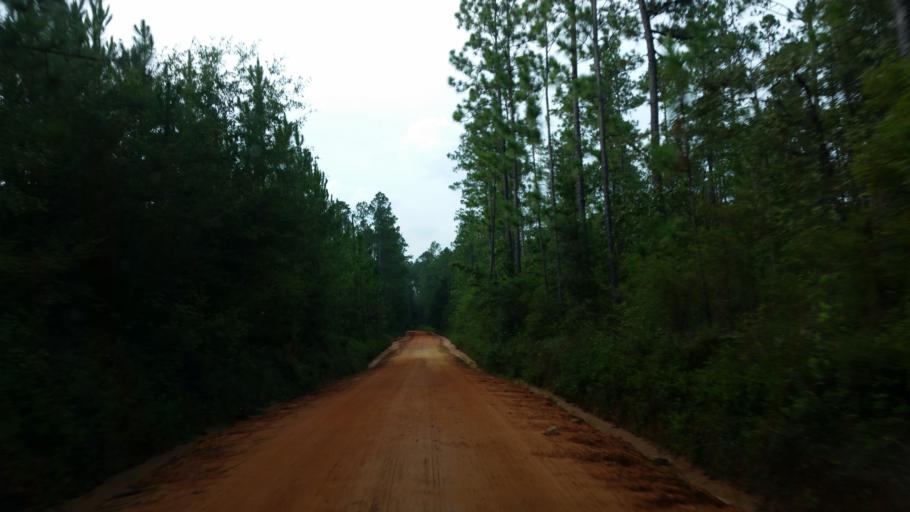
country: US
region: Alabama
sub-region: Baldwin County
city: Bay Minette
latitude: 30.7993
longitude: -87.5605
